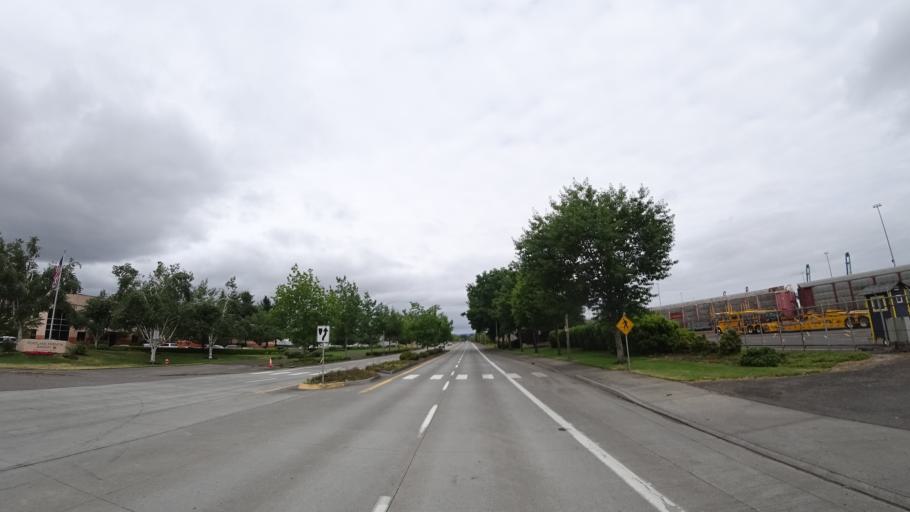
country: US
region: Washington
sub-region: Clark County
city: Lake Shore
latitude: 45.6301
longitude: -122.7448
